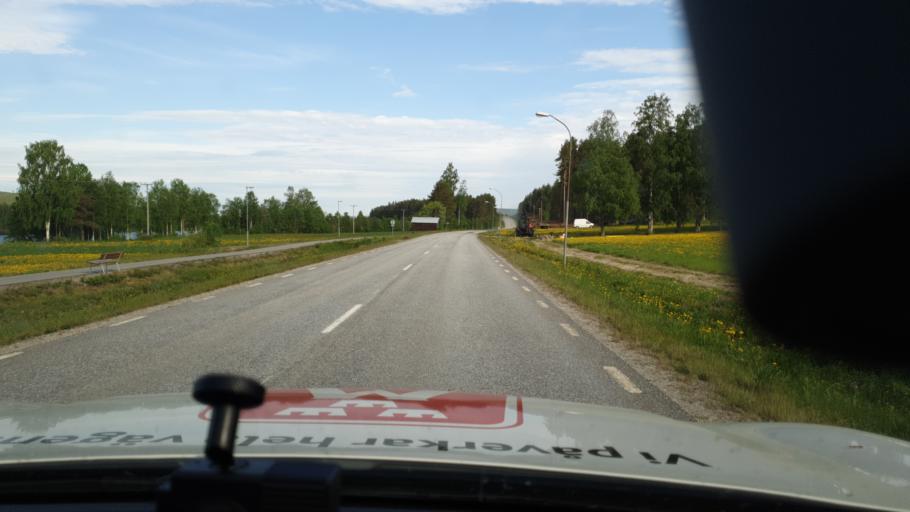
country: SE
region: Vaesterbotten
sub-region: Bjurholms Kommun
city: Bjurholm
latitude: 64.2629
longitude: 19.2792
